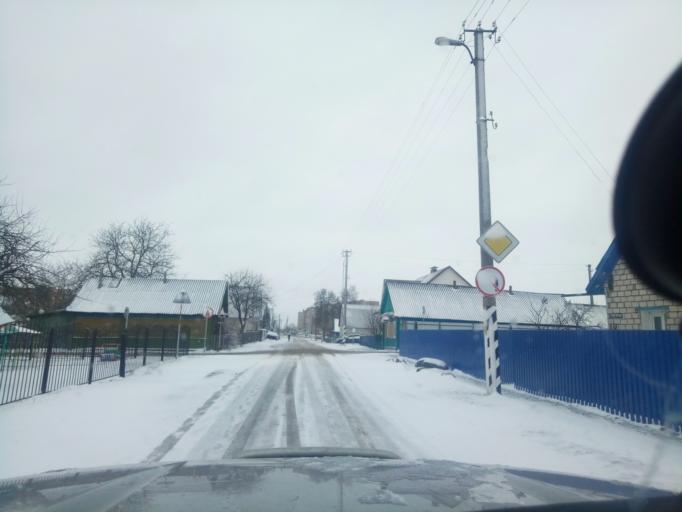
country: BY
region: Minsk
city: Kapyl'
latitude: 53.1531
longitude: 27.0829
